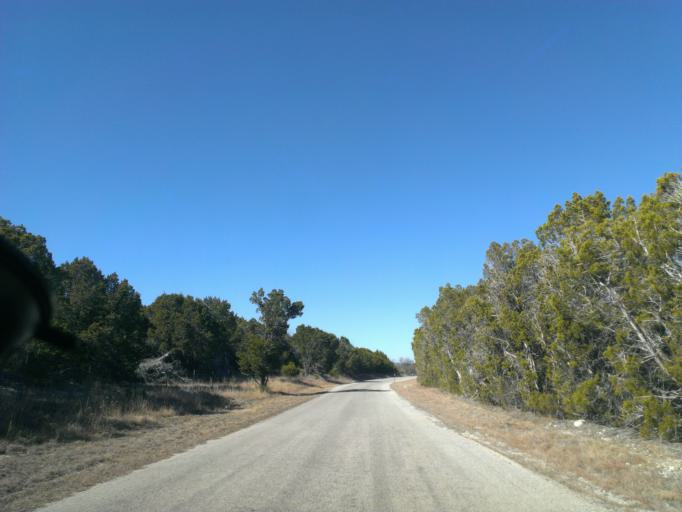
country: US
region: Texas
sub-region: Lampasas County
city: Lampasas
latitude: 30.9212
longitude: -98.1329
